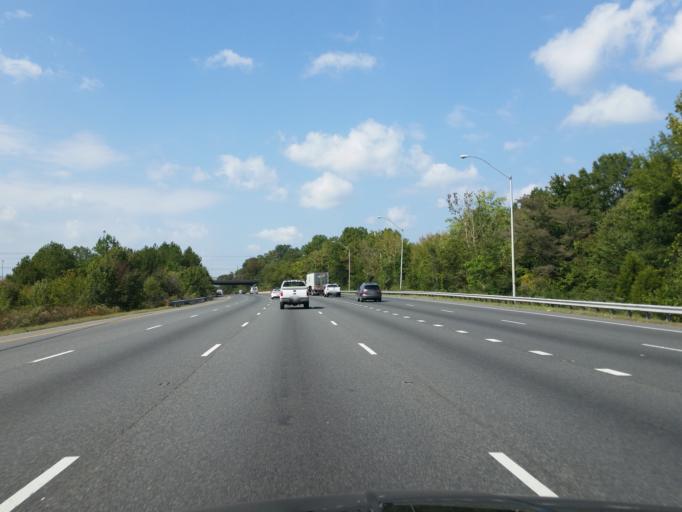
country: US
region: Maryland
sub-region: Prince George's County
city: Beltsville
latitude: 39.0213
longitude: -76.9358
